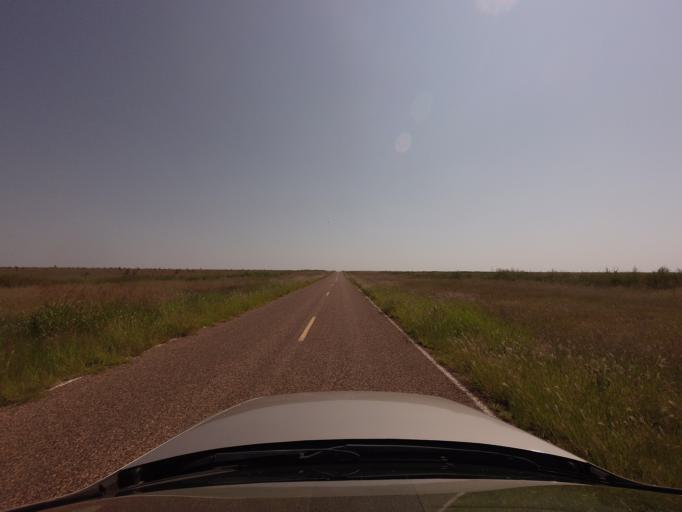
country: US
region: New Mexico
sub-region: Curry County
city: Cannon Air Force Base
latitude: 34.6330
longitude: -103.4005
